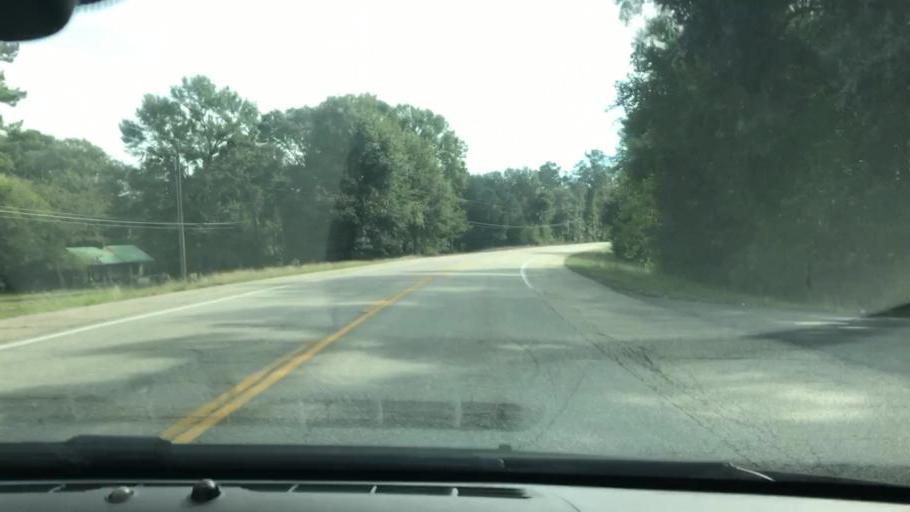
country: US
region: Mississippi
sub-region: Pearl River County
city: Nicholson
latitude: 30.5132
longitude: -89.8244
